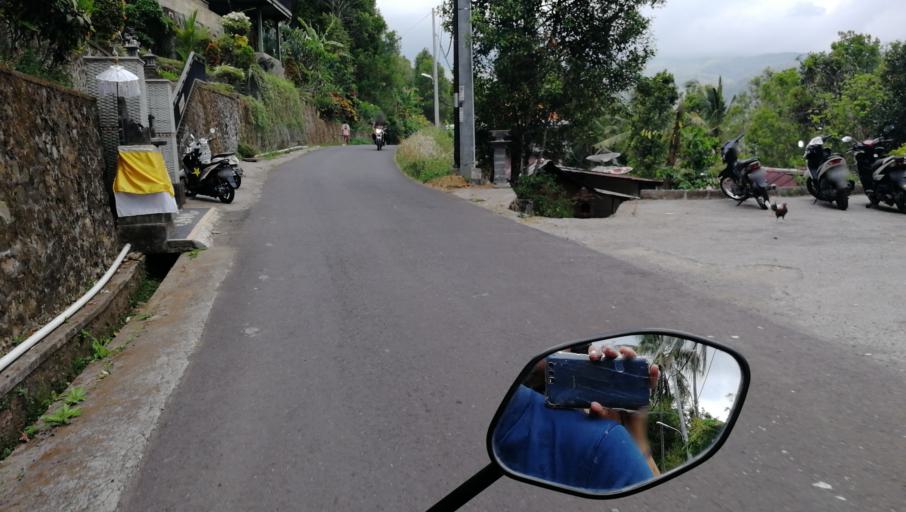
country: ID
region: Bali
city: Banjar Pedawa
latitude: -8.2644
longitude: 115.0417
